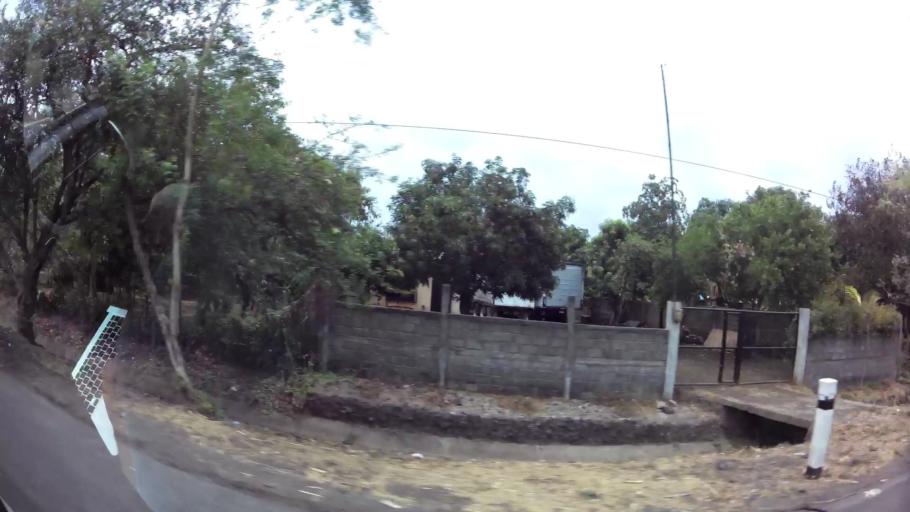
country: NI
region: Leon
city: Telica
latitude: 12.5253
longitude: -86.8772
